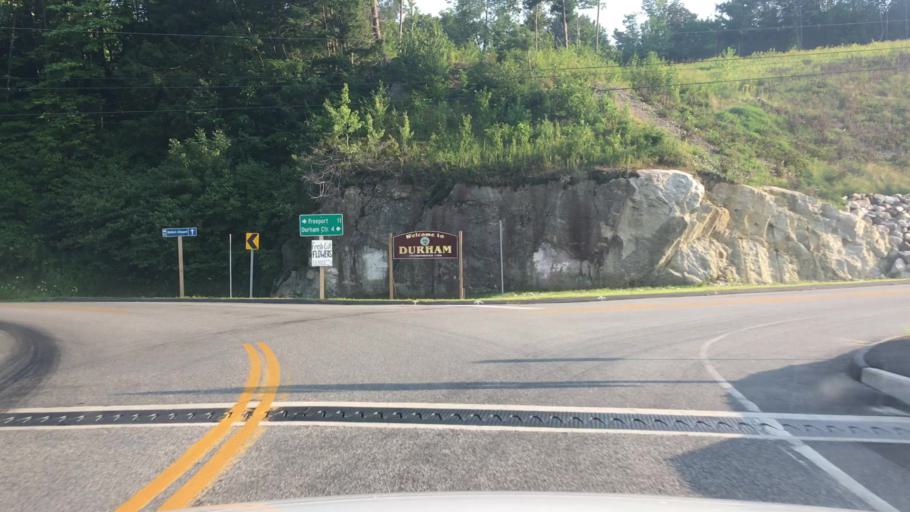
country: US
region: Maine
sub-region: Androscoggin County
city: Lisbon Falls
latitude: 43.9927
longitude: -70.0586
